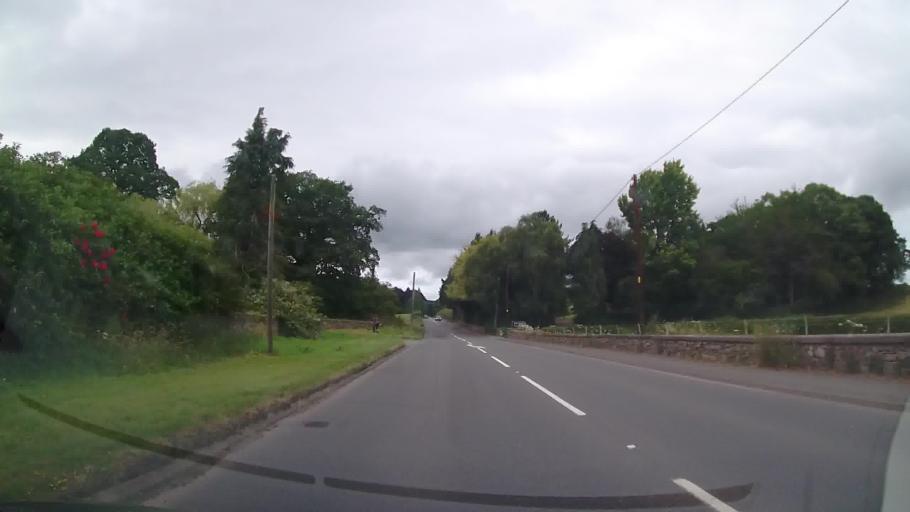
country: GB
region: Wales
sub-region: Wrexham
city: Chirk
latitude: 52.9575
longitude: -3.0699
